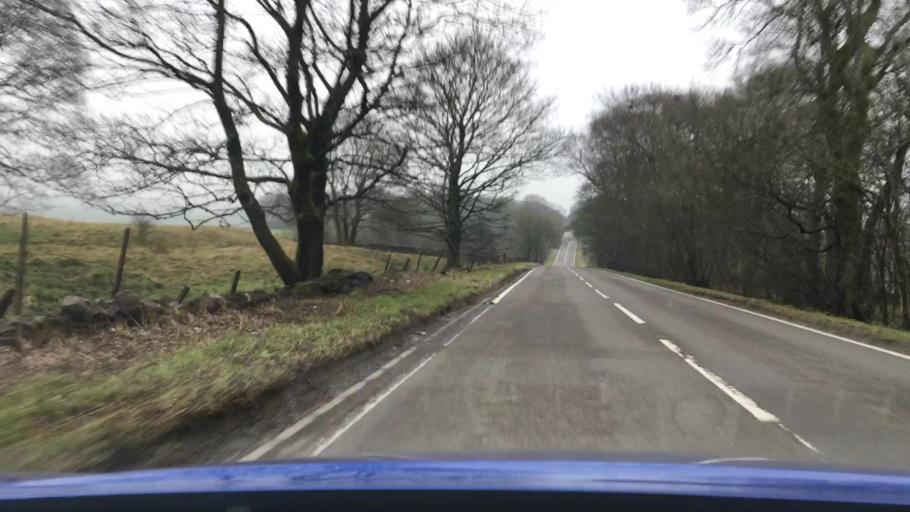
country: GB
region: England
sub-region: Derbyshire
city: High Peak
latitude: 53.3152
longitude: -1.8445
